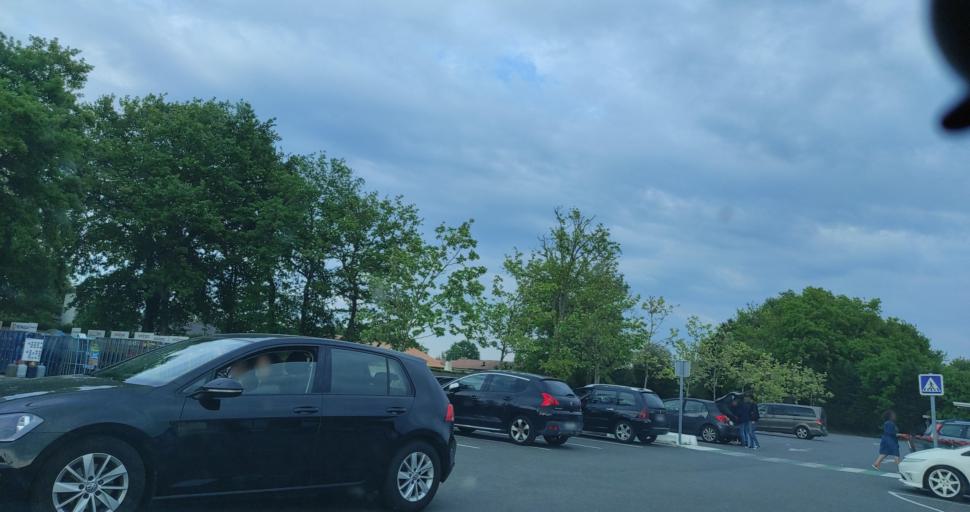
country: FR
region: Aquitaine
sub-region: Departement de la Gironde
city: Lanton
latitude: 44.7030
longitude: -1.0392
